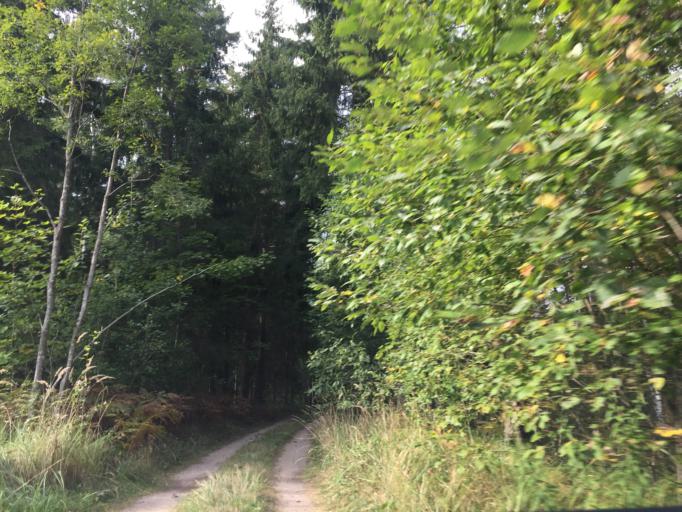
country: LV
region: Ikskile
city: Ikskile
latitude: 56.7621
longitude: 24.4699
